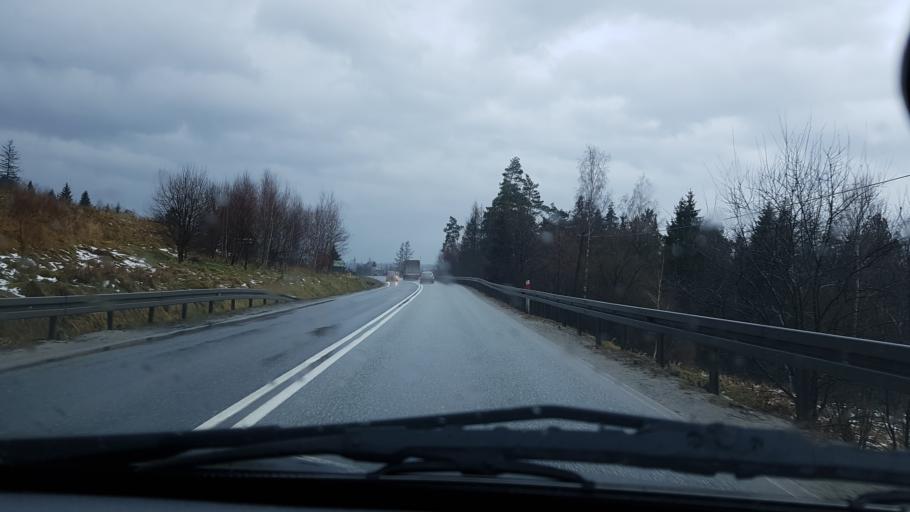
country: PL
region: Lesser Poland Voivodeship
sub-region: Powiat suski
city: Bystra
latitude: 49.6614
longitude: 19.8019
